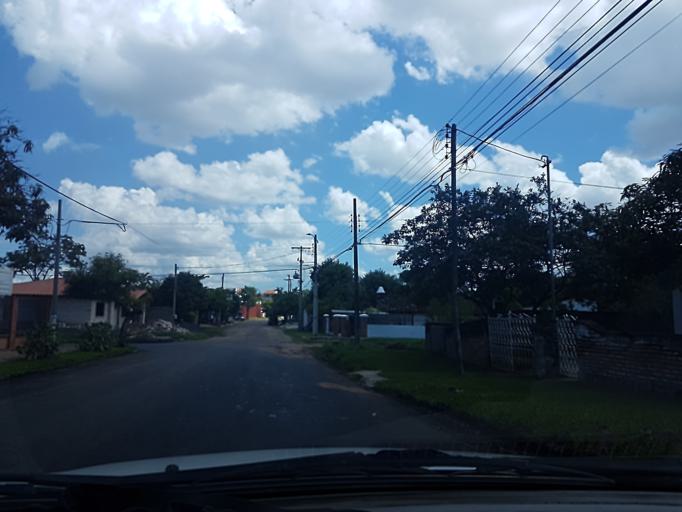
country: PY
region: Central
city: San Lorenzo
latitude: -25.2626
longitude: -57.5017
